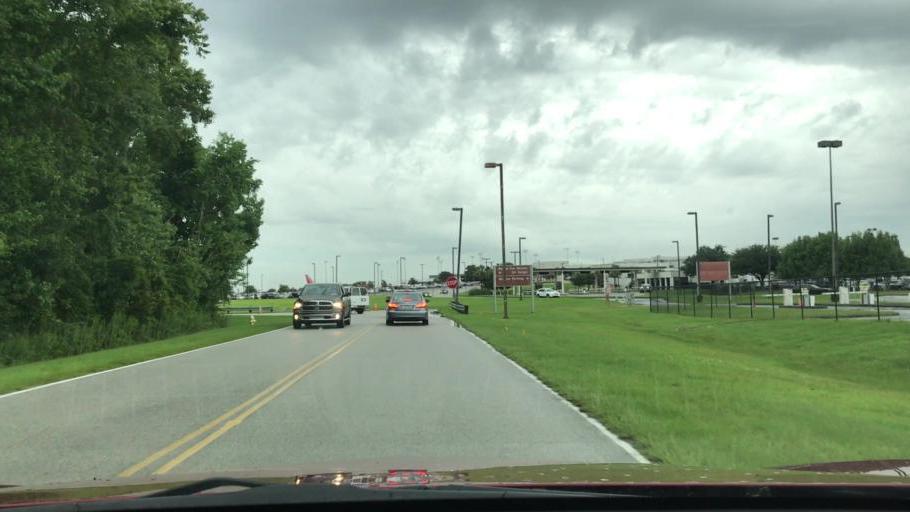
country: US
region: South Carolina
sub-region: Berkeley County
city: Hanahan
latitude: 32.8812
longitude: -80.0406
